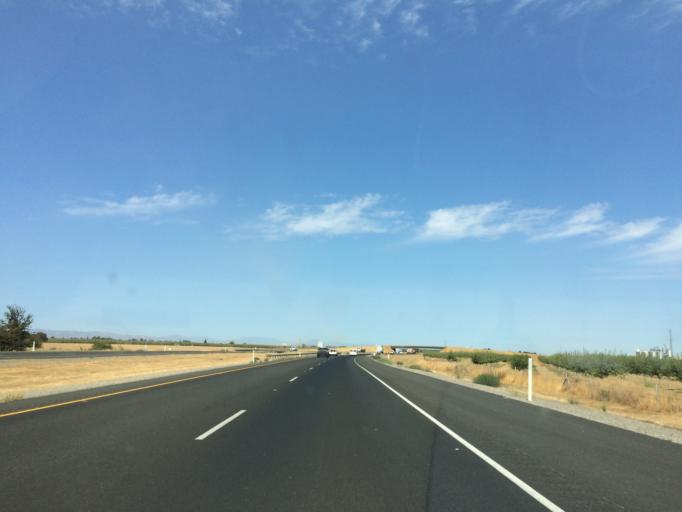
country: US
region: California
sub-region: Yolo County
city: Dunnigan
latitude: 38.9508
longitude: -122.0145
